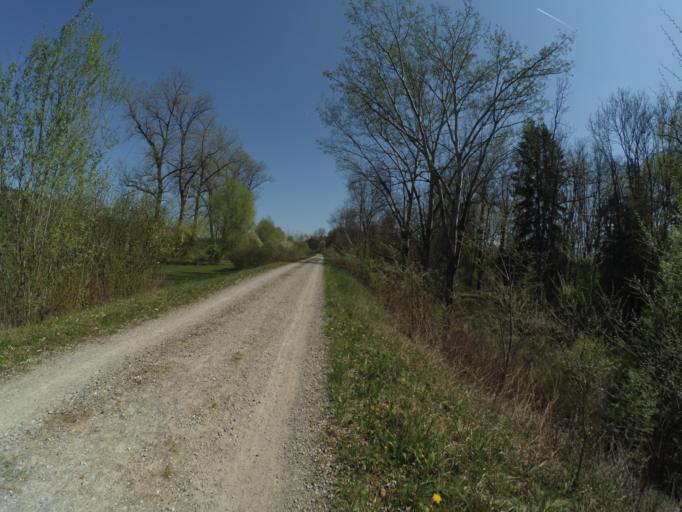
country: CH
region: Thurgau
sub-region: Frauenfeld District
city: Huttwilen
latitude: 47.5769
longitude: 8.8500
